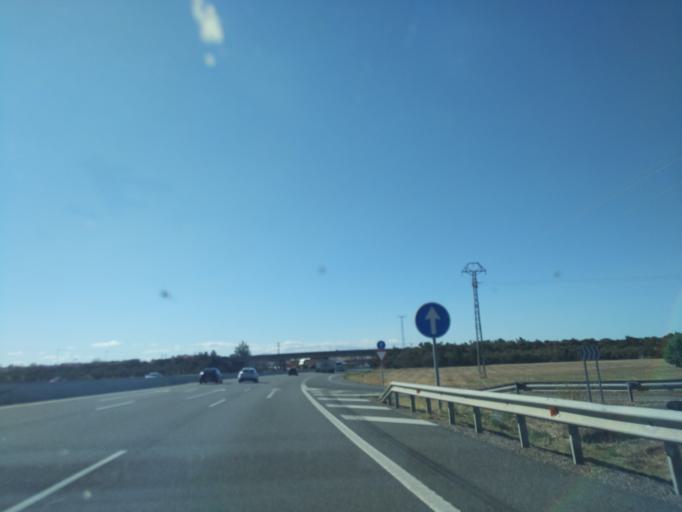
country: ES
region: Castille and Leon
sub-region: Provincia de Zamora
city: Benavente
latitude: 41.9983
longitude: -5.6545
